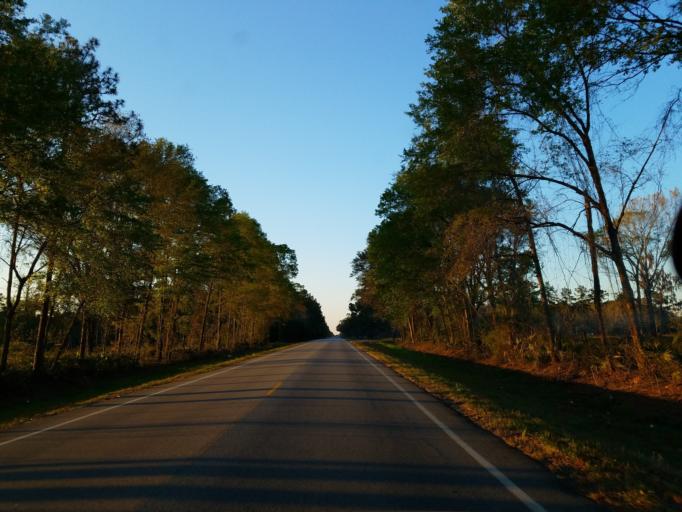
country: US
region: Georgia
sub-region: Lanier County
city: Lakeland
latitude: 30.9807
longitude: -83.0079
